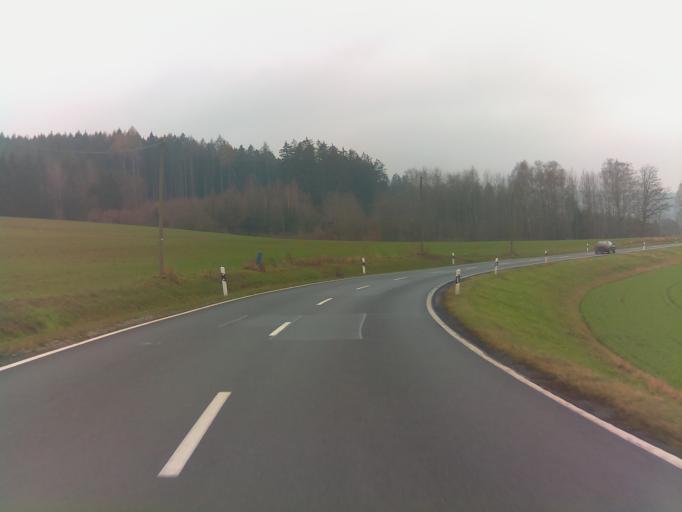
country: DE
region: Thuringia
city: Schleusingen
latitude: 50.4908
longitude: 10.7105
